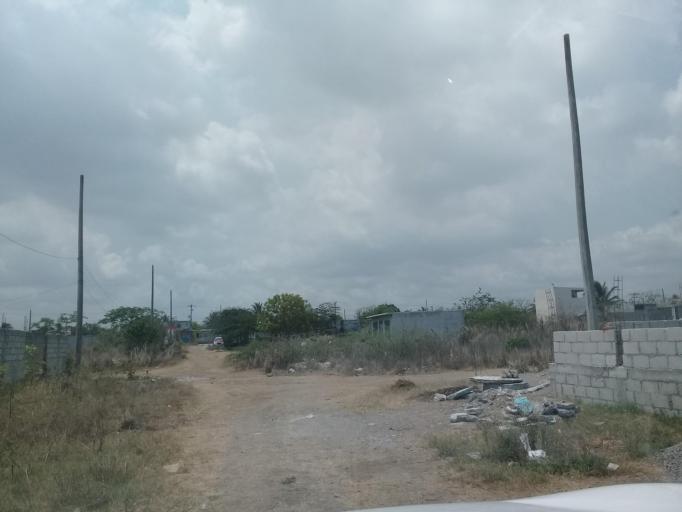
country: MX
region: Veracruz
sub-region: Veracruz
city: Las Amapolas
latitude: 19.1411
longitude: -96.2349
